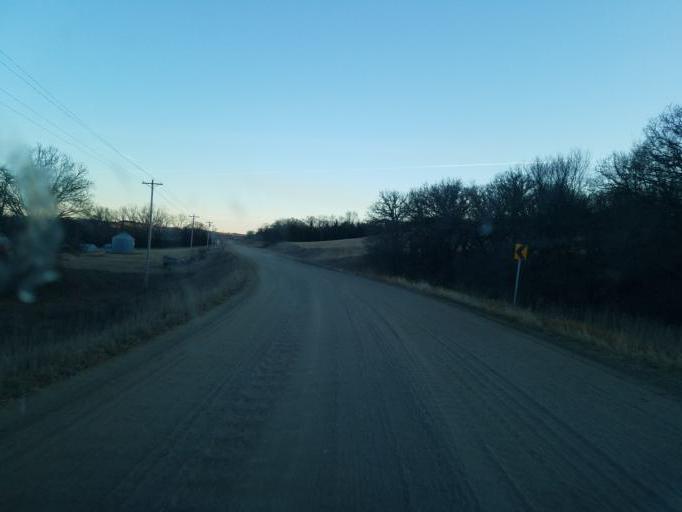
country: US
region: Nebraska
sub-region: Knox County
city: Center
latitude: 42.6767
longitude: -97.8969
